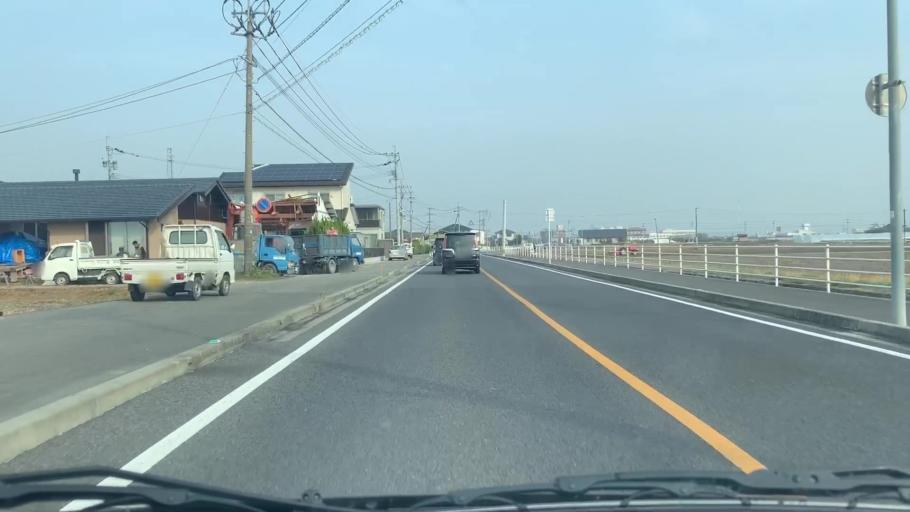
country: JP
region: Saga Prefecture
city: Saga-shi
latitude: 33.2334
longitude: 130.2575
